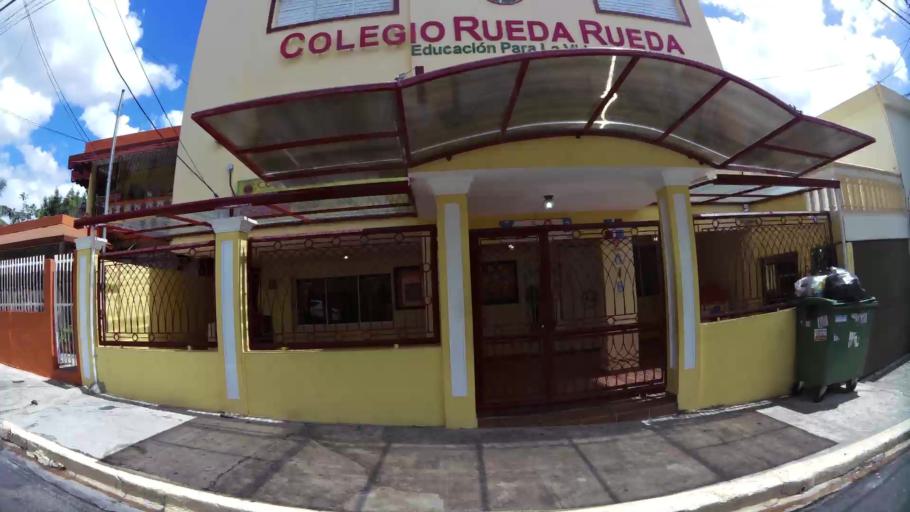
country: DO
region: Nacional
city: Ensanche Luperon
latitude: 18.5205
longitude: -69.9136
